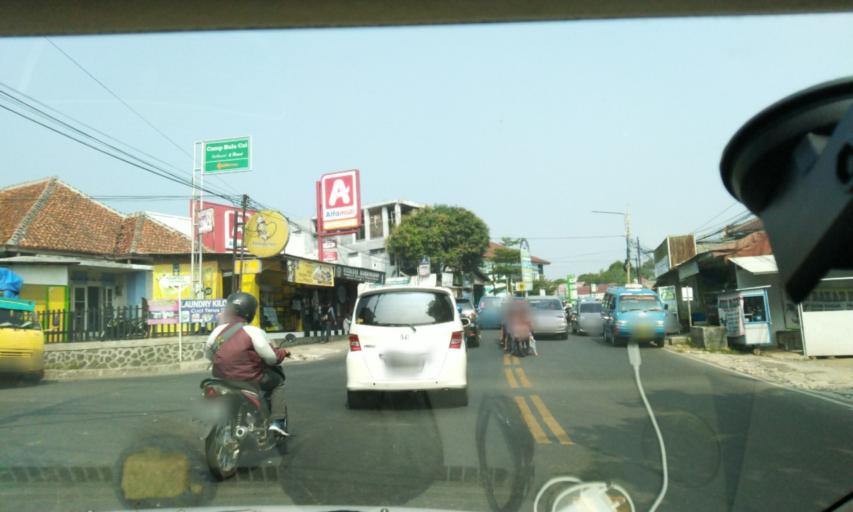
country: ID
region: West Java
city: Caringin
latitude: -6.6630
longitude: 106.8563
